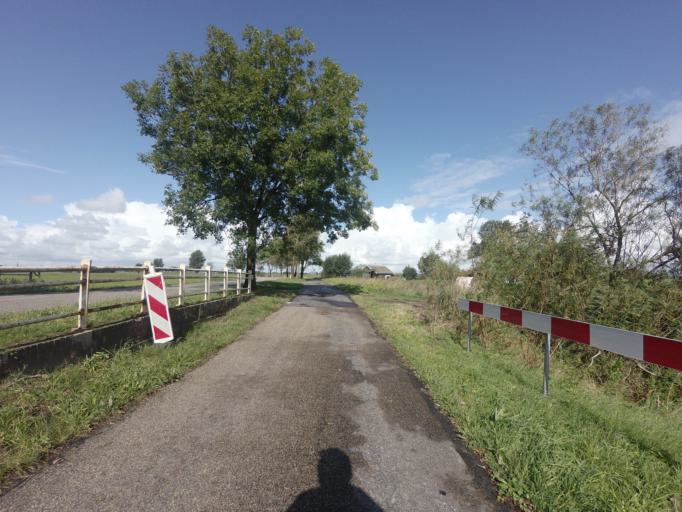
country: NL
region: Friesland
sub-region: Gemeente Boarnsterhim
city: Warten
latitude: 53.1511
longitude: 5.8758
